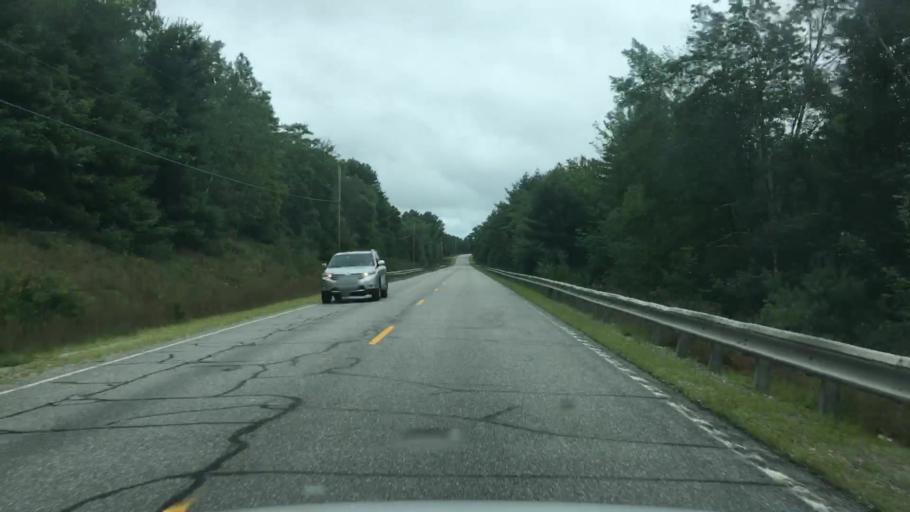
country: US
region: Maine
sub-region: Oxford County
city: Brownfield
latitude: 43.9181
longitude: -70.8566
